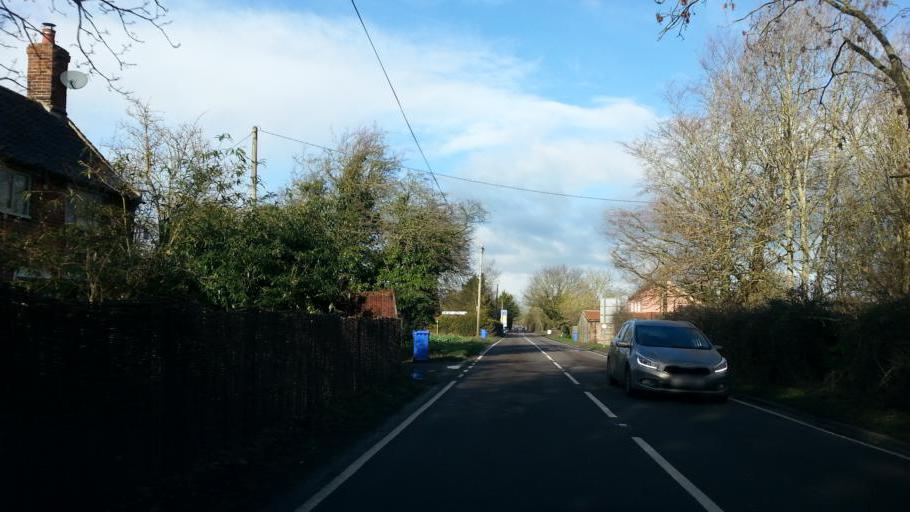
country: GB
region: England
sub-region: Suffolk
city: Halesworth
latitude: 52.3936
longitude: 1.4989
